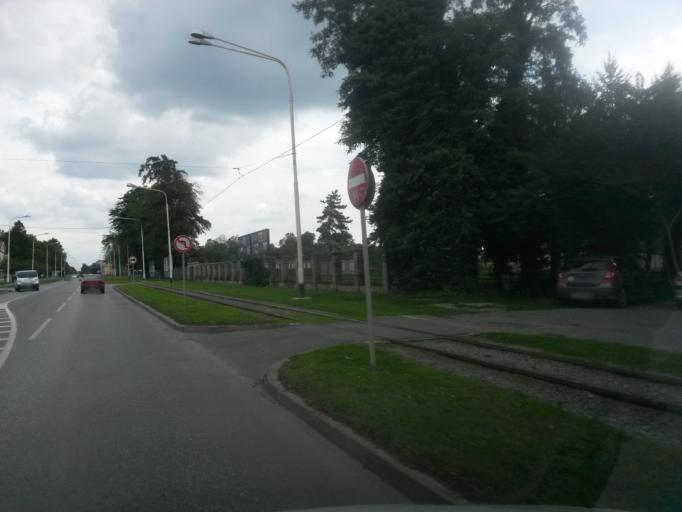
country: HR
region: Osjecko-Baranjska
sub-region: Grad Osijek
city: Osijek
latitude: 45.5580
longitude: 18.7076
